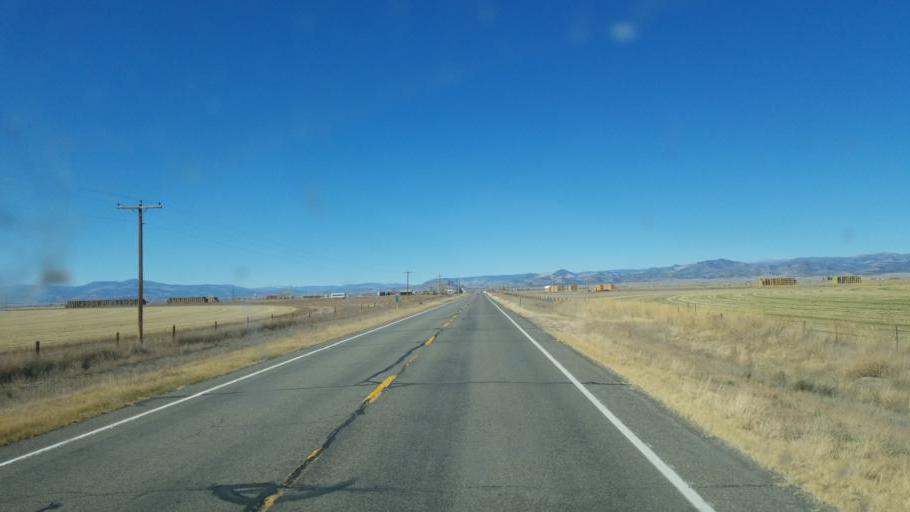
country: US
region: Colorado
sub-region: Saguache County
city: Center
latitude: 37.7482
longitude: -106.1529
